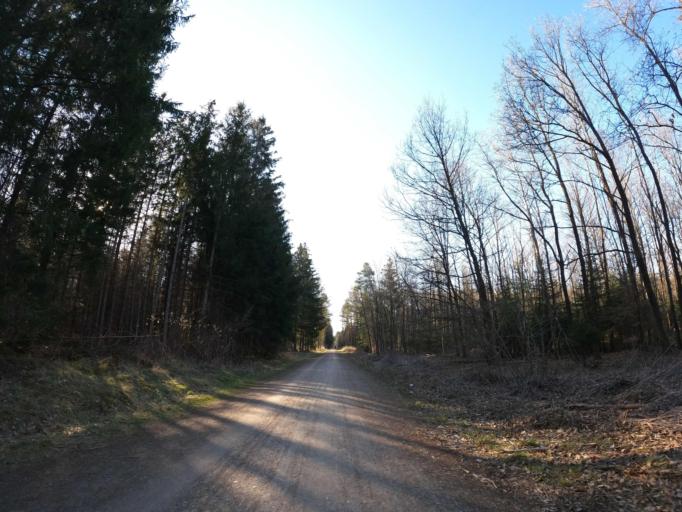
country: DE
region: Bavaria
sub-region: Upper Bavaria
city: Unterhaching
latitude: 48.0734
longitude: 11.5843
